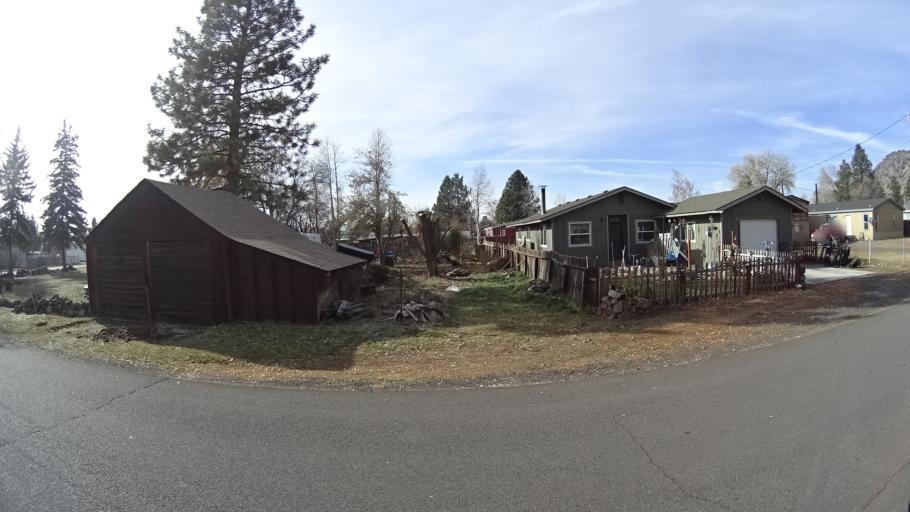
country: US
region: Oregon
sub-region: Klamath County
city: Klamath Falls
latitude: 41.9690
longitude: -121.9157
